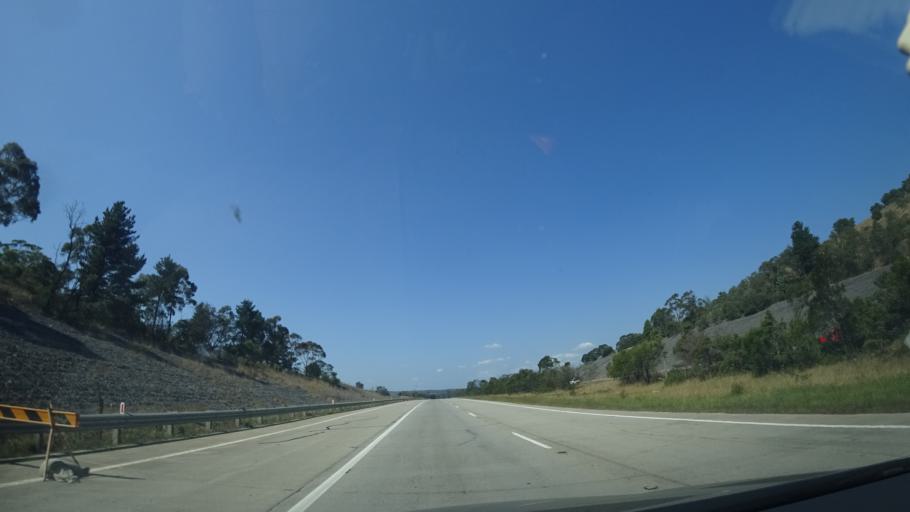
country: AU
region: New South Wales
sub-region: Wingecarribee
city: Bowral
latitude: -34.4546
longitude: 150.3644
